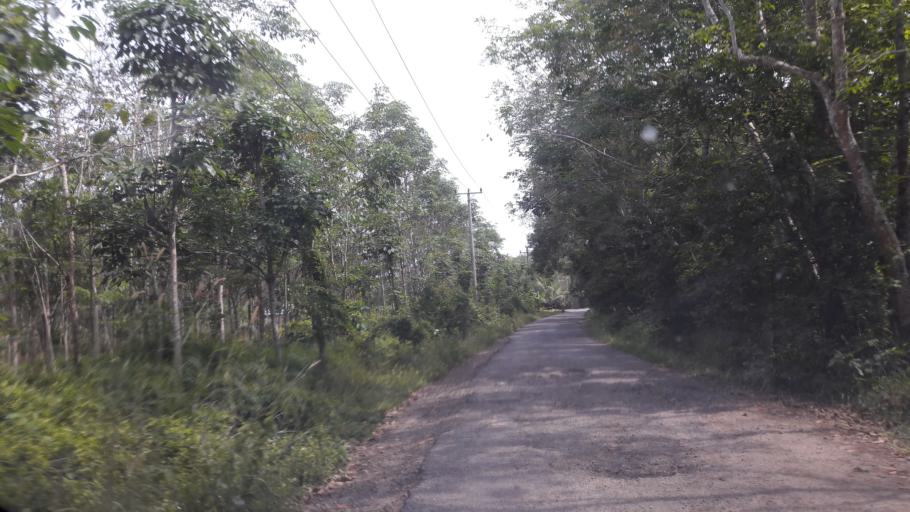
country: ID
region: South Sumatra
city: Gunungmenang
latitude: -3.2247
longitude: 104.1063
